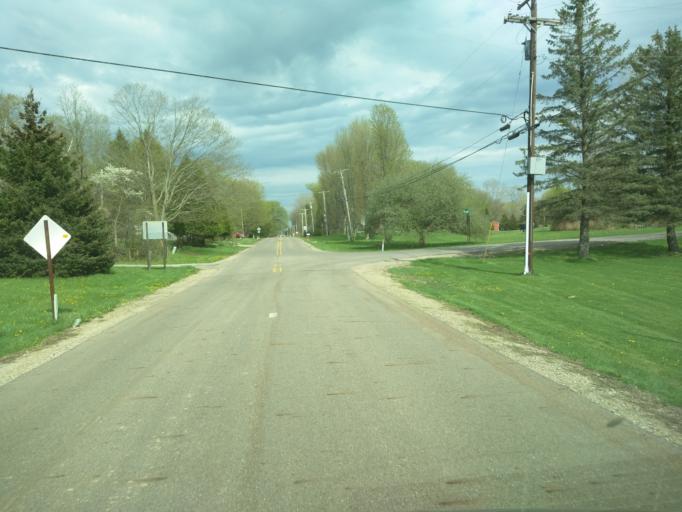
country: US
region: Michigan
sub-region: Eaton County
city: Dimondale
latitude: 42.6831
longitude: -84.6233
